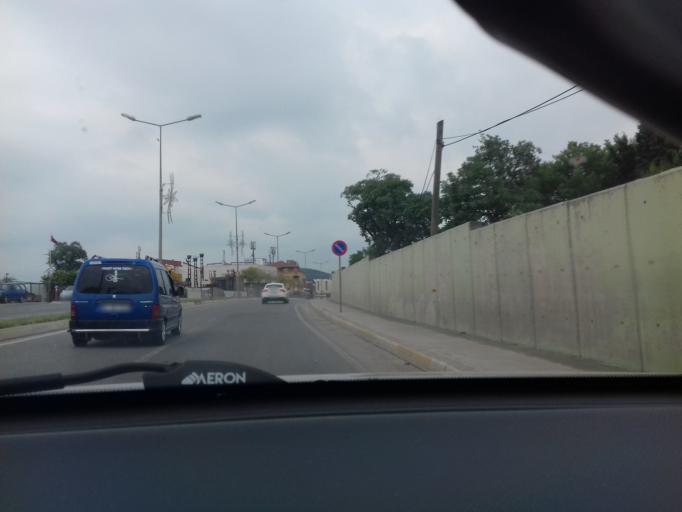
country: TR
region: Istanbul
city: Icmeler
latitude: 40.8921
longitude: 29.3545
